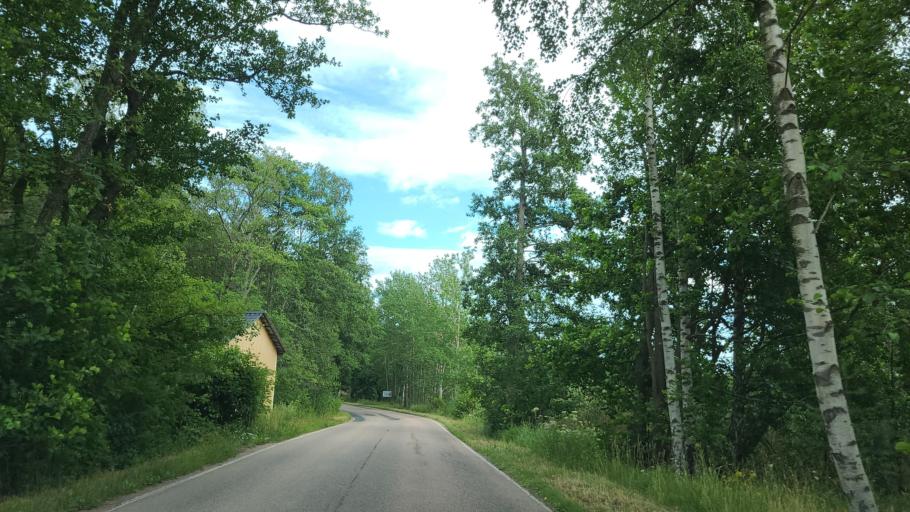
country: FI
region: Varsinais-Suomi
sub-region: Turku
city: Rymaettylae
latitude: 60.3457
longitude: 21.9591
